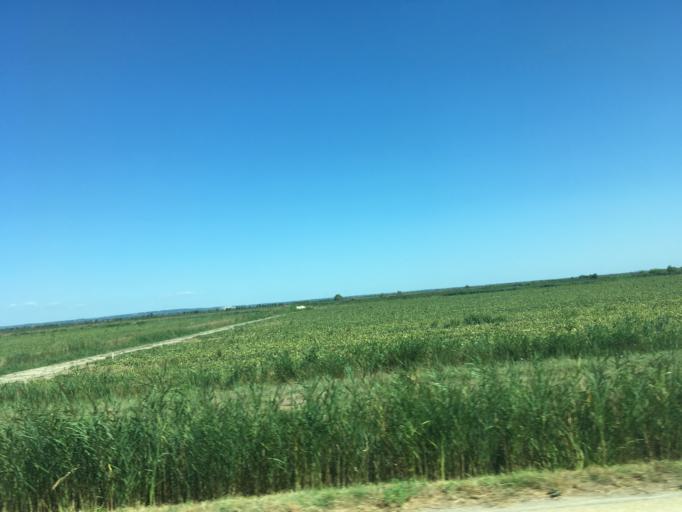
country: FR
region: Languedoc-Roussillon
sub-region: Departement du Gard
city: Saint-Gilles
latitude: 43.6234
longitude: 4.5170
